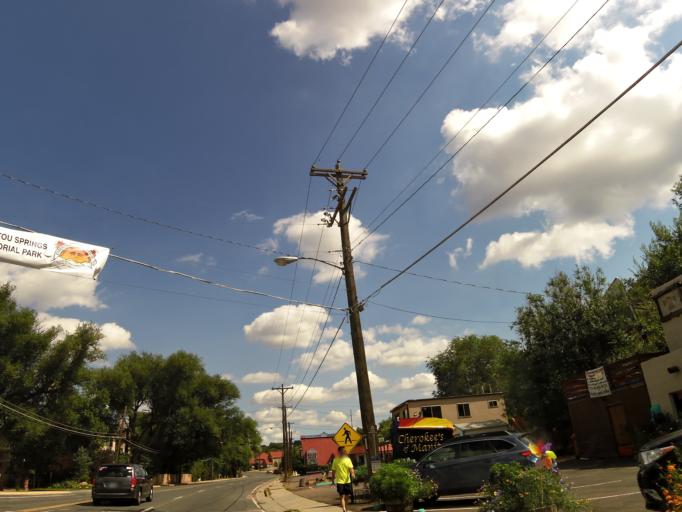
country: US
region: Colorado
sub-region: El Paso County
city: Manitou Springs
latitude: 38.8575
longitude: -104.9035
